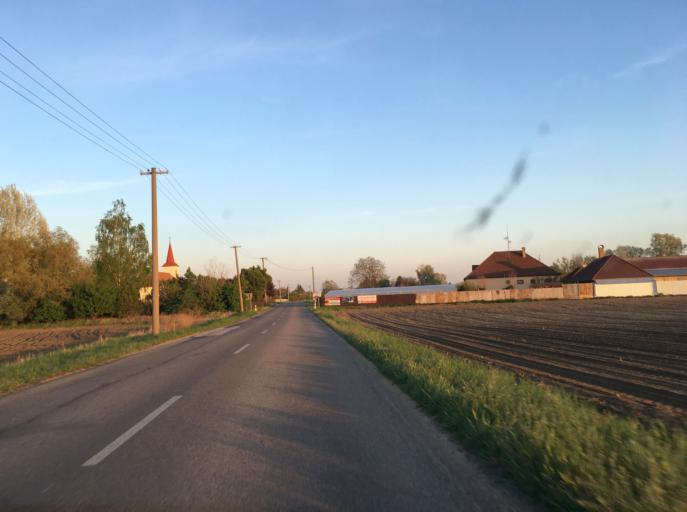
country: SK
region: Nitriansky
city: Kolarovo
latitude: 47.8927
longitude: 17.8936
